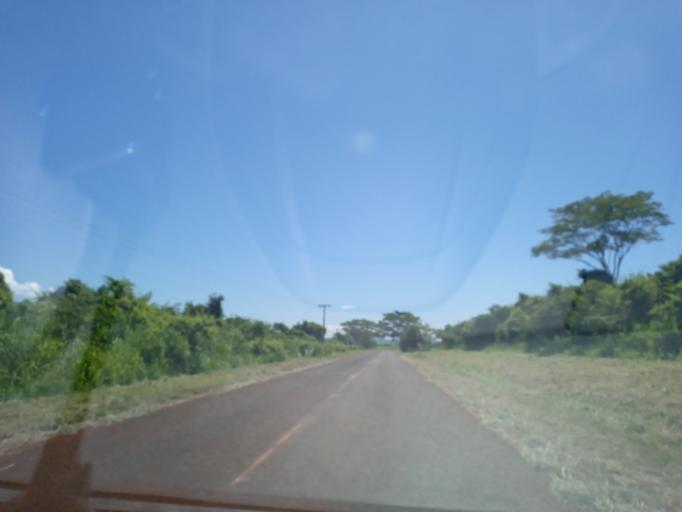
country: BR
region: Goias
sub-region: Itumbiara
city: Itumbiara
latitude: -18.4142
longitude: -49.1312
